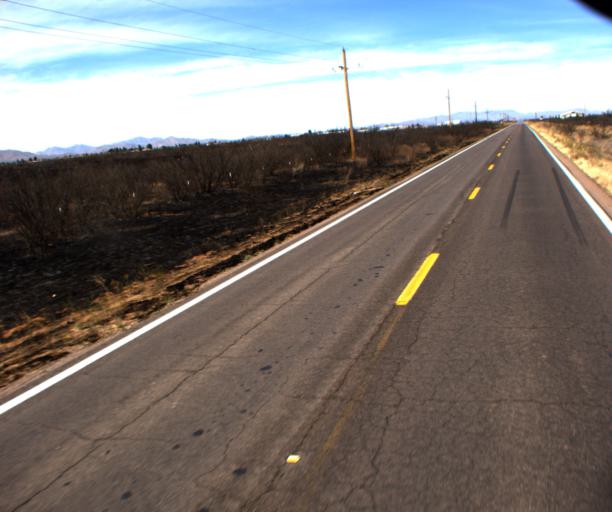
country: US
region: Arizona
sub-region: Cochise County
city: Willcox
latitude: 31.9806
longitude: -109.8512
